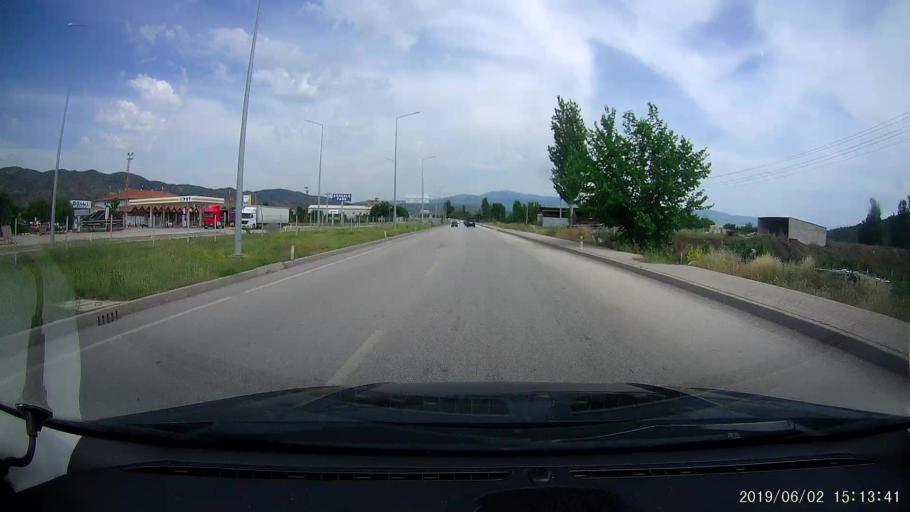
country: TR
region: Corum
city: Osmancik
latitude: 40.9711
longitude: 34.8242
